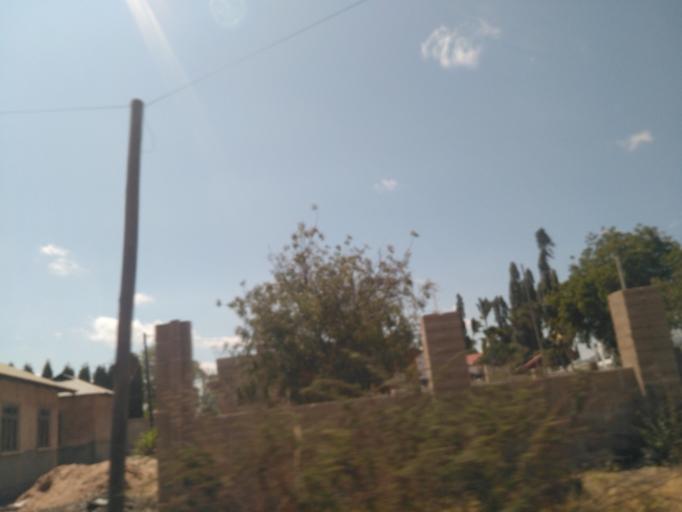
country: TZ
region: Dodoma
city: Dodoma
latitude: -6.1676
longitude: 35.7591
